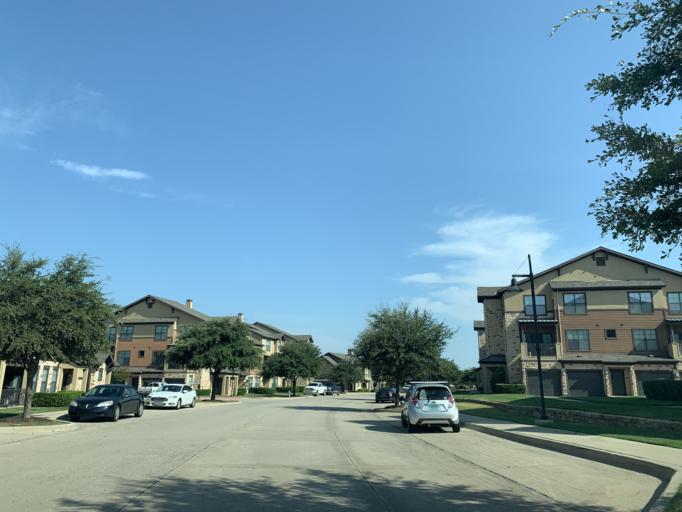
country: US
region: Texas
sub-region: Tarrant County
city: Blue Mound
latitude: 32.8931
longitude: -97.3118
